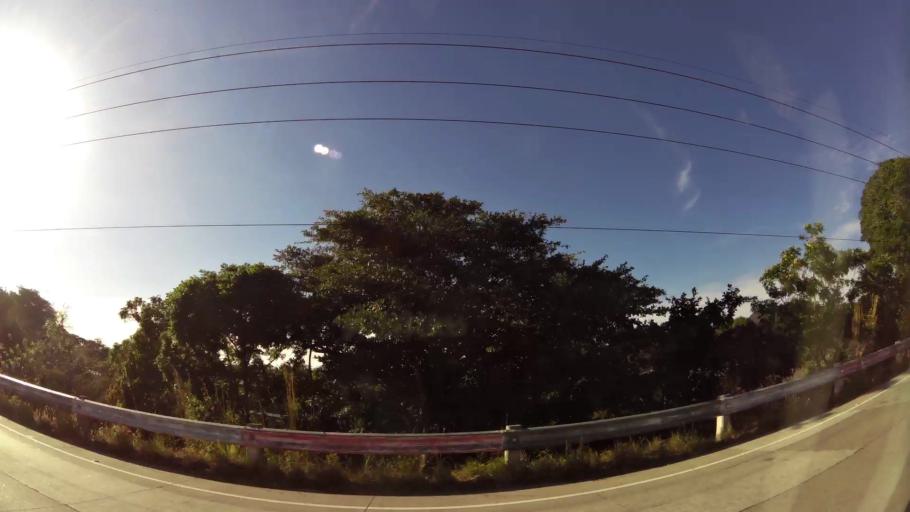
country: SV
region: Santa Ana
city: Metapan
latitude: 14.2427
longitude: -89.4722
